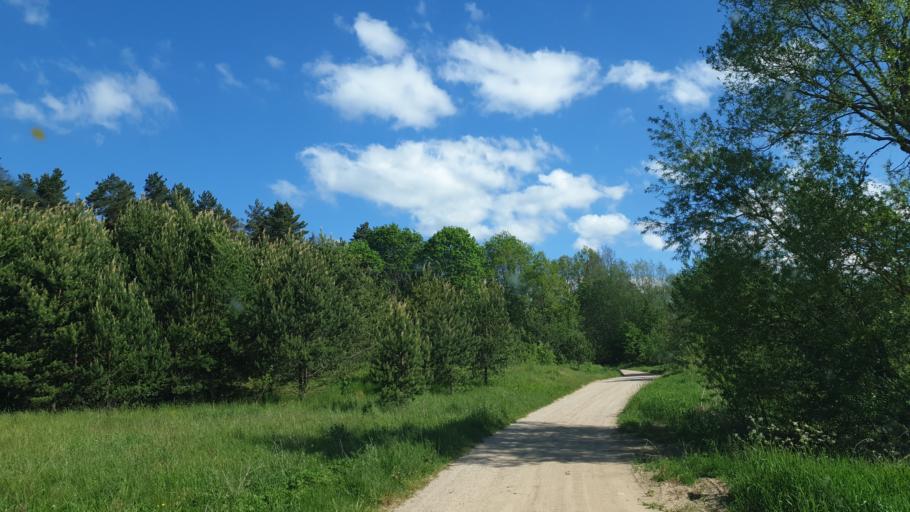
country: LT
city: Aukstadvaris
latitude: 54.5791
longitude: 24.4598
